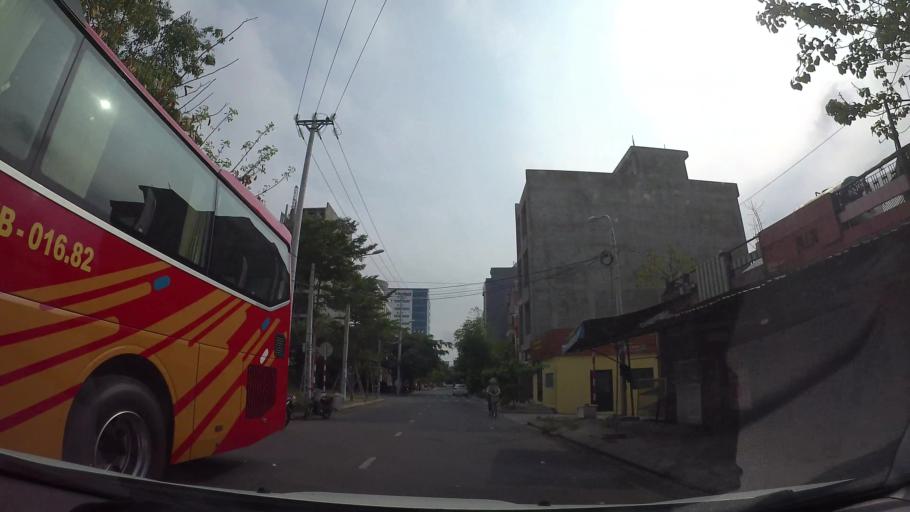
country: VN
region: Da Nang
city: Son Tra
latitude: 16.0714
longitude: 108.2340
